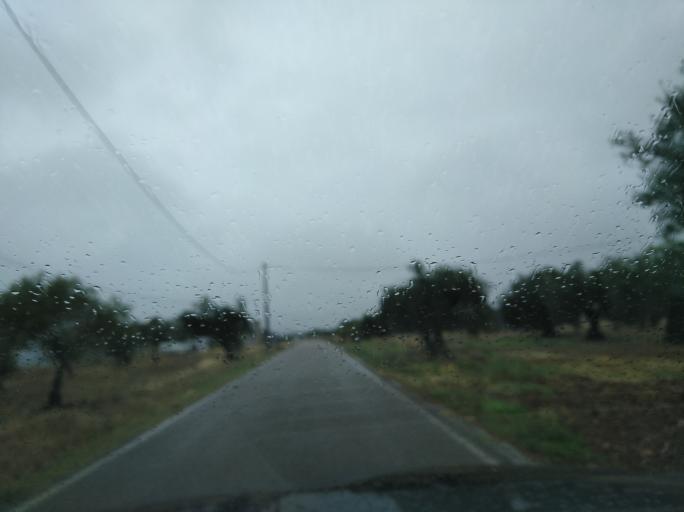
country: PT
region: Portalegre
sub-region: Campo Maior
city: Campo Maior
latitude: 38.9597
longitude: -7.0797
